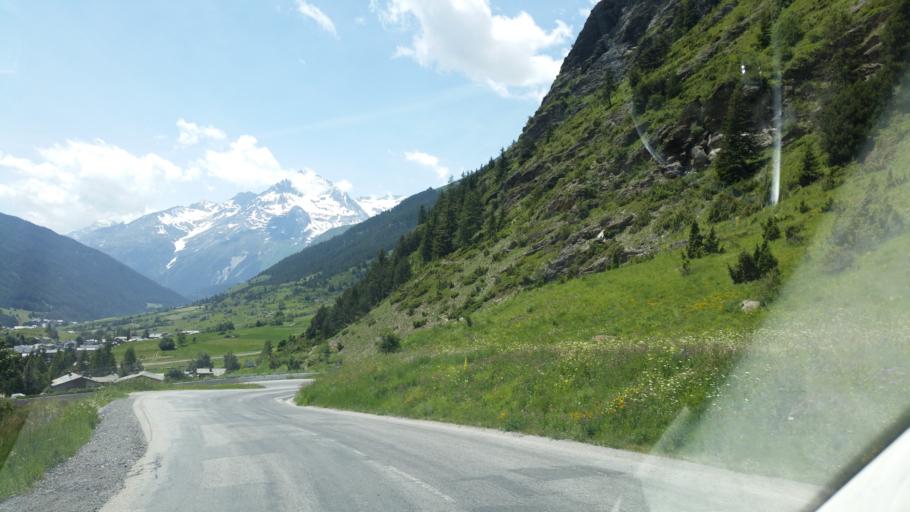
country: IT
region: Piedmont
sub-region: Provincia di Torino
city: Moncenisio
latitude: 45.2942
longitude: 6.9255
